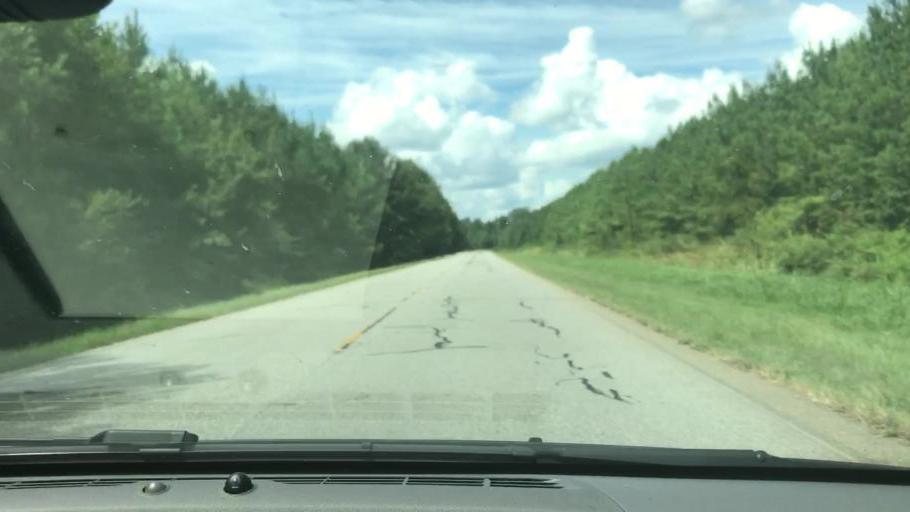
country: US
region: Georgia
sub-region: Stewart County
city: Lumpkin
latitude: 32.1442
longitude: -84.8827
